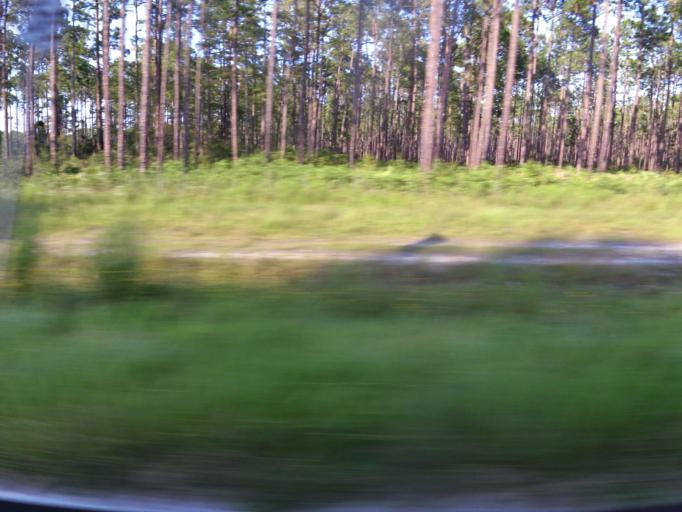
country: US
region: Florida
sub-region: Duval County
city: Baldwin
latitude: 30.3891
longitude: -82.0260
